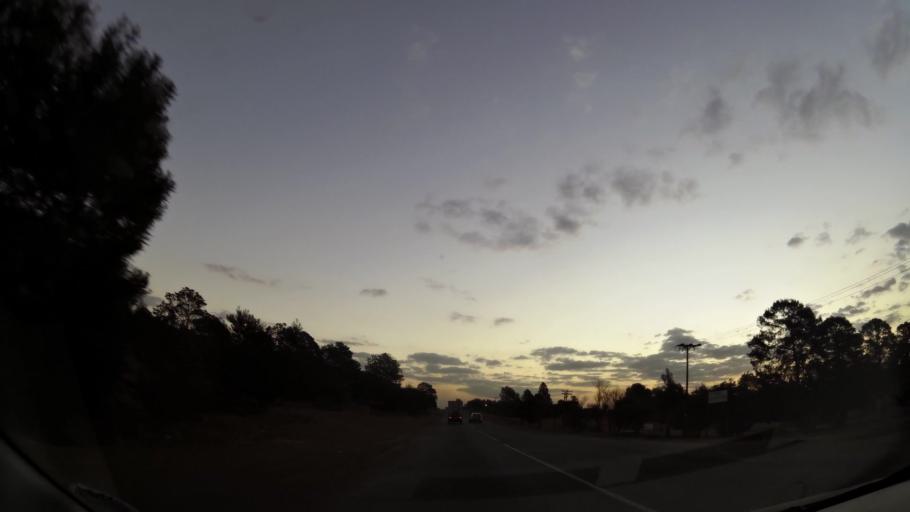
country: ZA
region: Gauteng
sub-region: West Rand District Municipality
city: Krugersdorp
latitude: -26.0694
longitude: 27.6804
